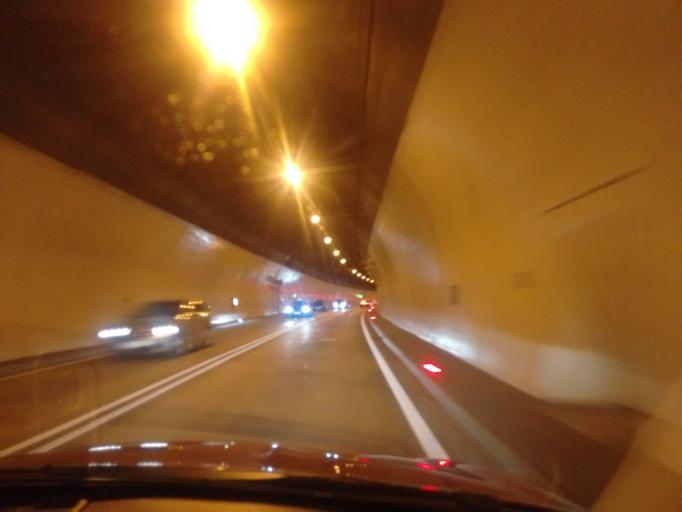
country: AT
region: Upper Austria
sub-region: Politischer Bezirk Gmunden
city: Ebensee
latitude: 47.8450
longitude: 13.7808
